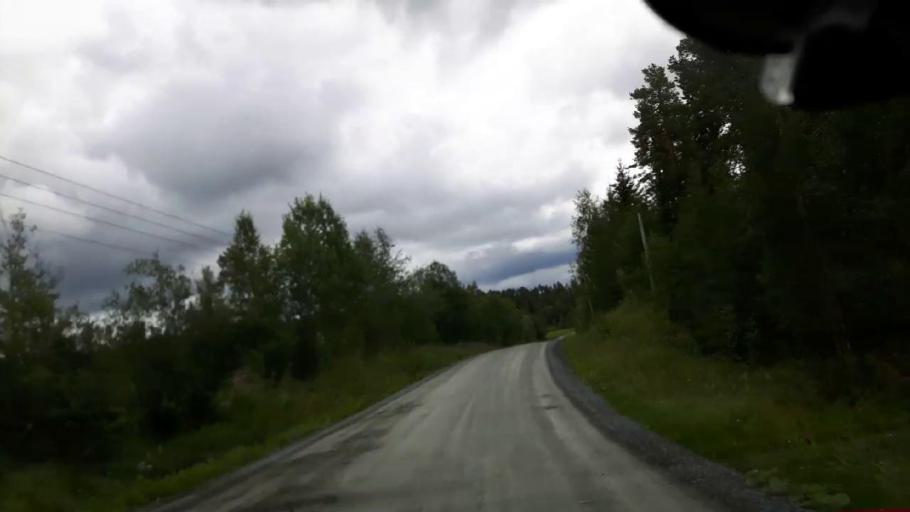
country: SE
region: Jaemtland
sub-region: Krokoms Kommun
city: Krokom
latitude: 63.5750
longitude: 14.2369
